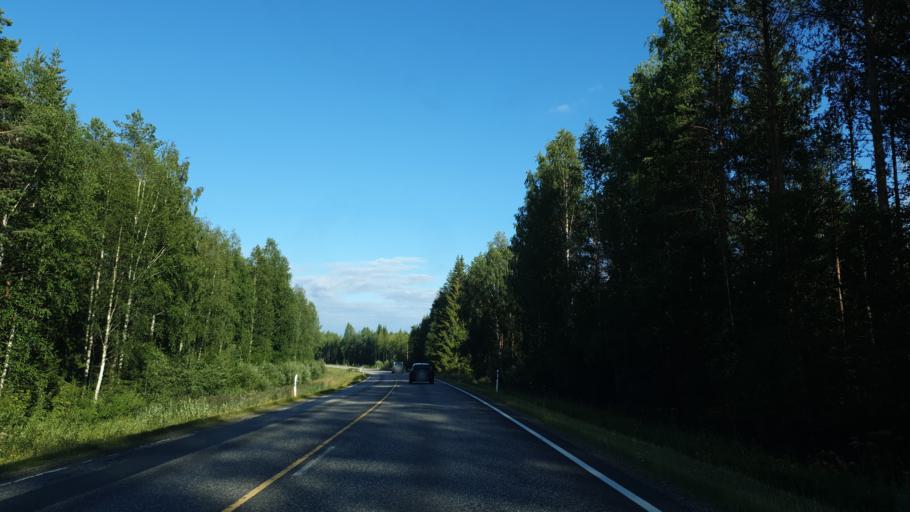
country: FI
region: North Karelia
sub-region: Joensuu
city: Outokumpu
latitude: 62.5205
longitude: 29.0096
